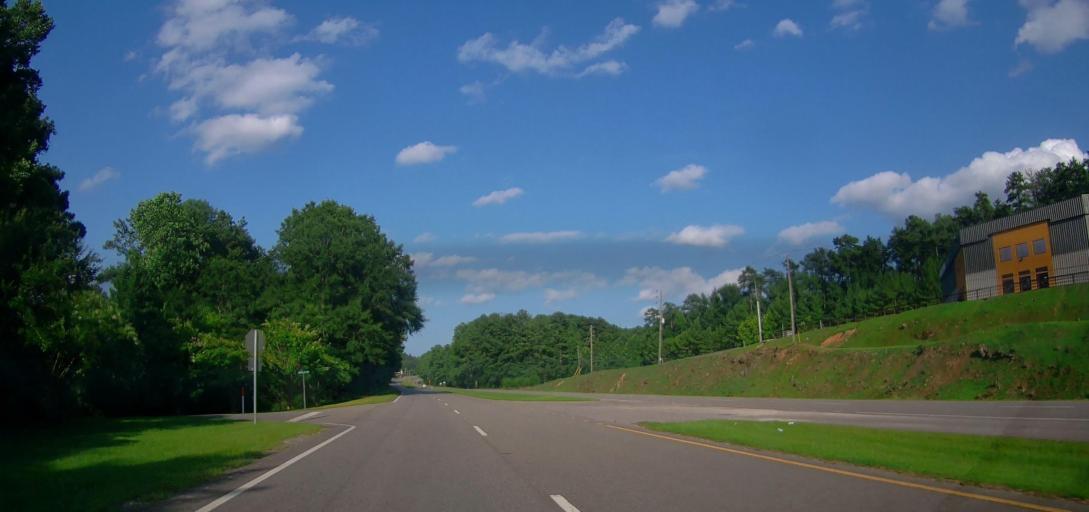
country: US
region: Alabama
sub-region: Jefferson County
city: Irondale
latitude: 33.5468
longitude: -86.6735
